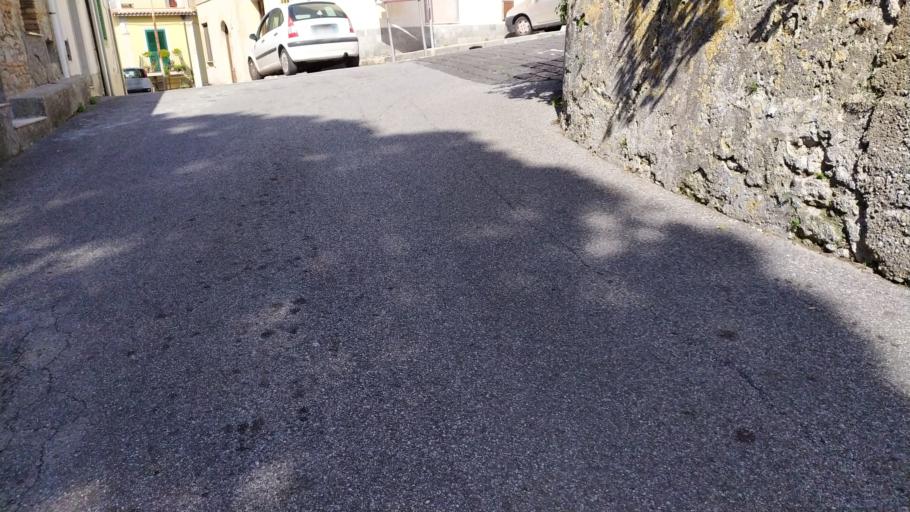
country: IT
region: Sicily
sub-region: Messina
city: Rometta
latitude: 38.1703
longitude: 15.4138
